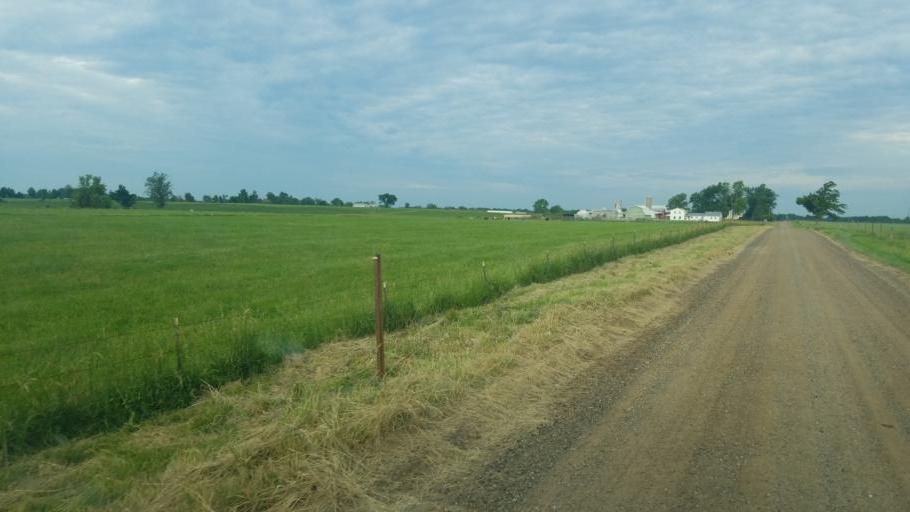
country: US
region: Michigan
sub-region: Eaton County
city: Charlotte
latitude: 42.5972
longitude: -84.9457
